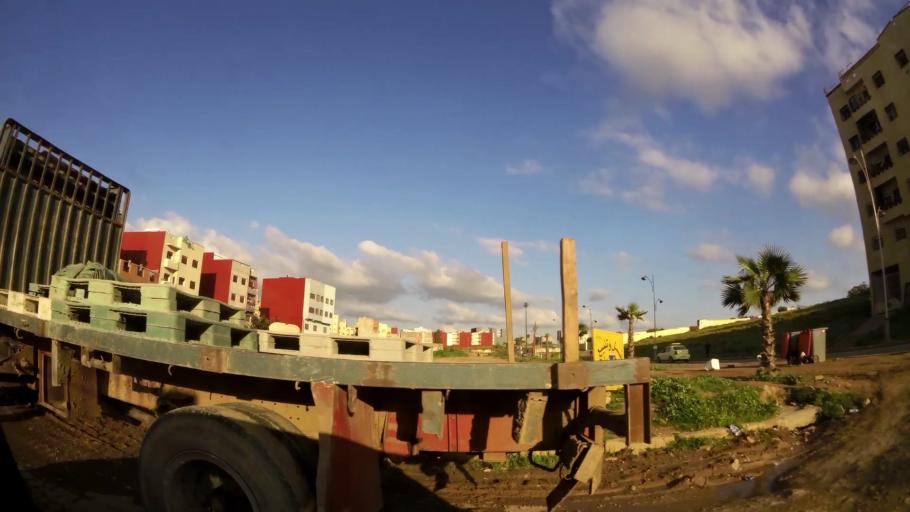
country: MA
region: Chaouia-Ouardigha
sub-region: Settat Province
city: Settat
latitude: 33.0024
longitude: -7.6054
